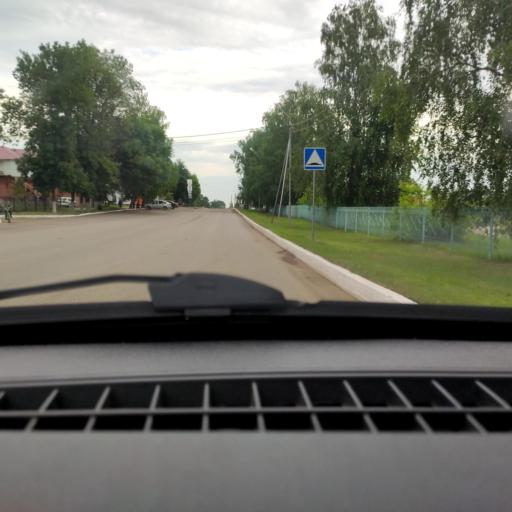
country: RU
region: Bashkortostan
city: Chishmy
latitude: 54.5869
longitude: 55.3833
